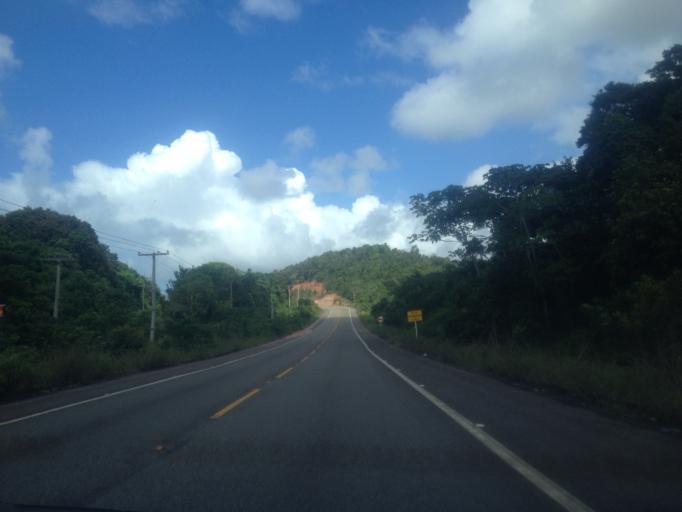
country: BR
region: Sergipe
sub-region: Indiaroba
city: Indiaroba
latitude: -11.4838
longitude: -37.4843
